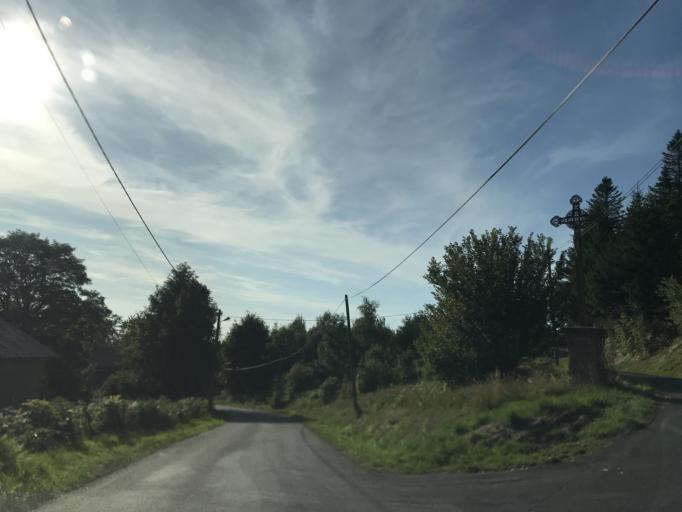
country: FR
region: Auvergne
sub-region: Departement du Puy-de-Dome
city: Job
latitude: 45.6763
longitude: 3.7430
